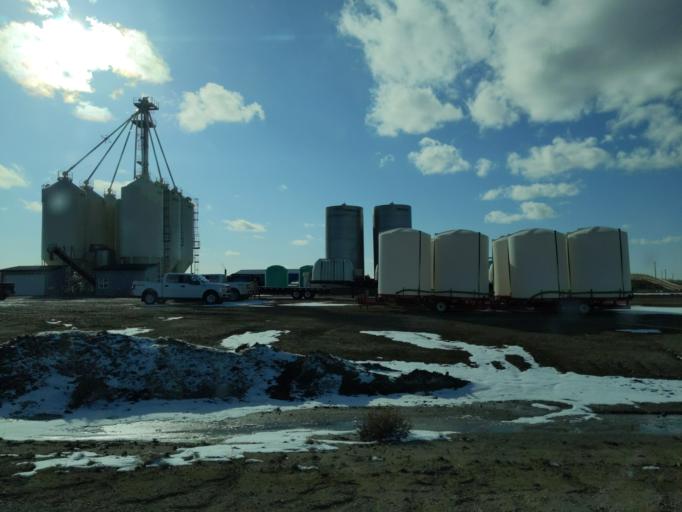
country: CA
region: Saskatchewan
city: Lloydminster
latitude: 53.2450
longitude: -109.9708
